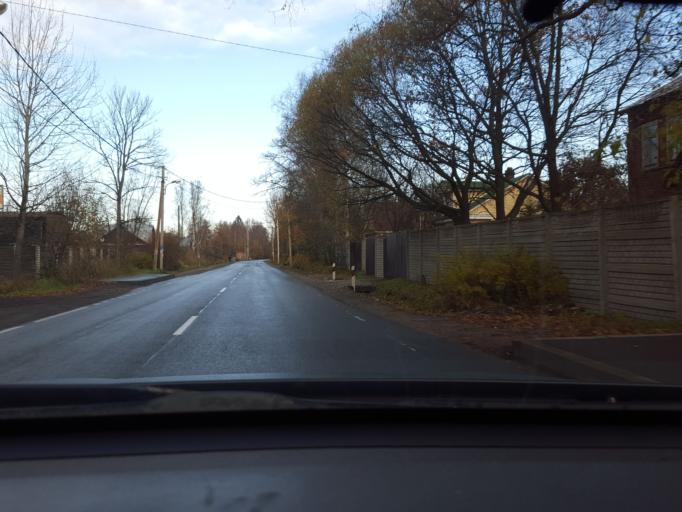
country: RU
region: St.-Petersburg
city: Shuvalovo
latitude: 60.0452
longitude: 30.2961
